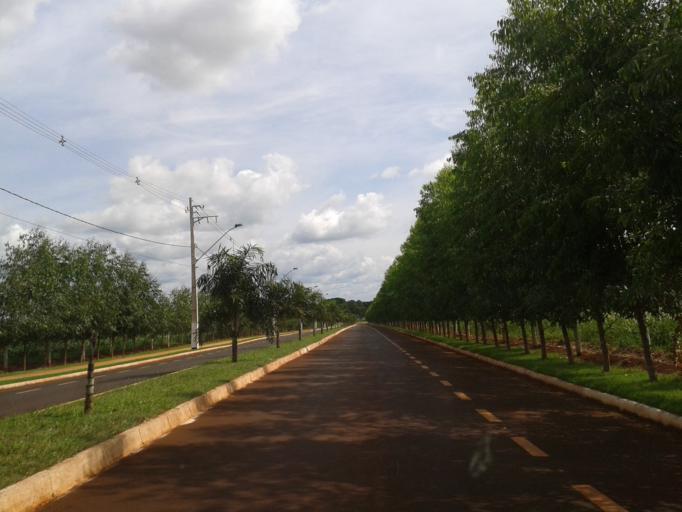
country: BR
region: Minas Gerais
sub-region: Centralina
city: Centralina
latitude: -18.5758
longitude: -49.1969
